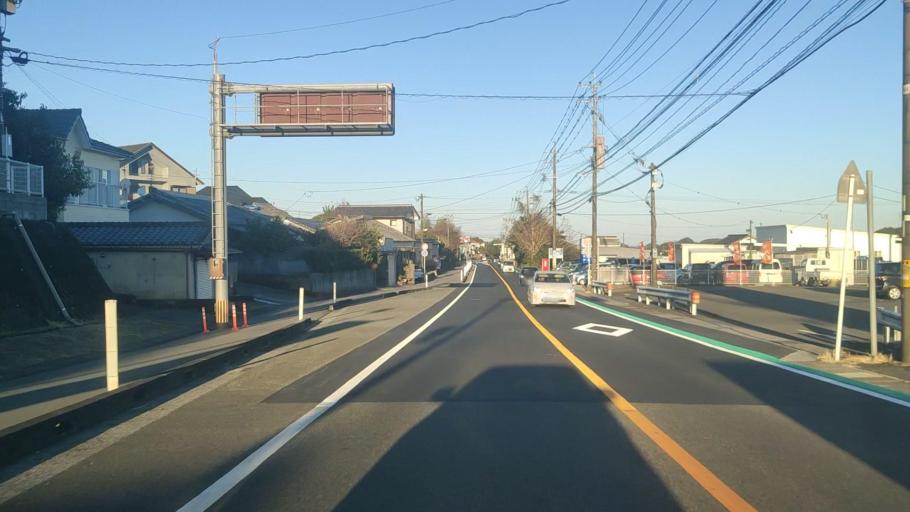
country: JP
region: Miyazaki
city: Miyazaki-shi
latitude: 31.8429
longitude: 131.3411
